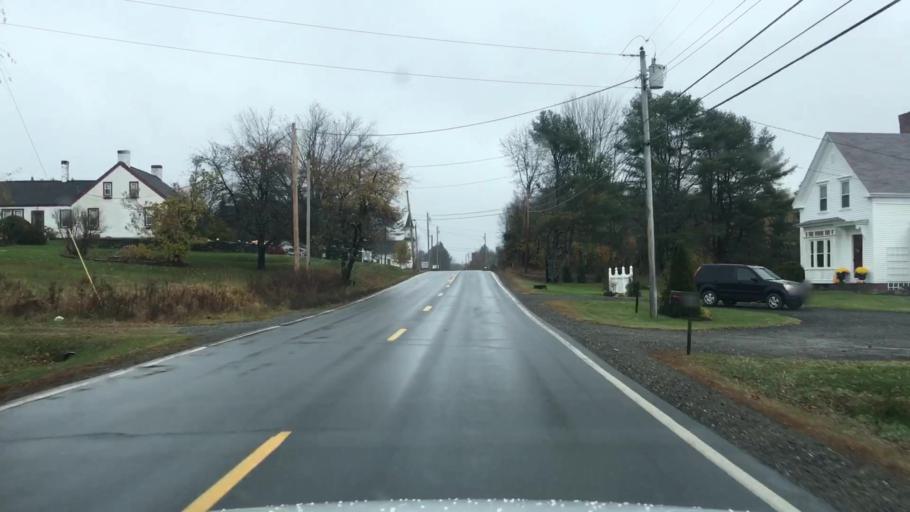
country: US
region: Maine
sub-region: Lincoln County
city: Jefferson
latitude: 44.1585
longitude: -69.4162
